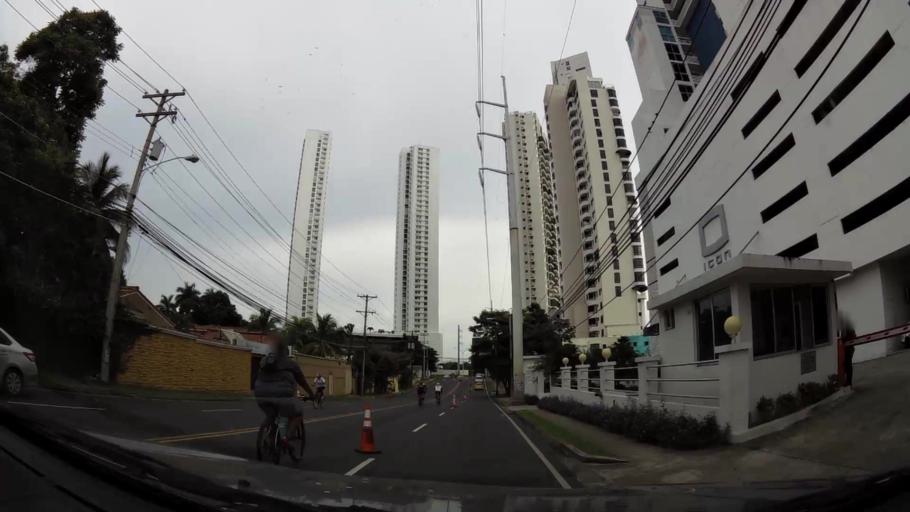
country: PA
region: Panama
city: Panama
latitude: 9.0019
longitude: -79.4961
